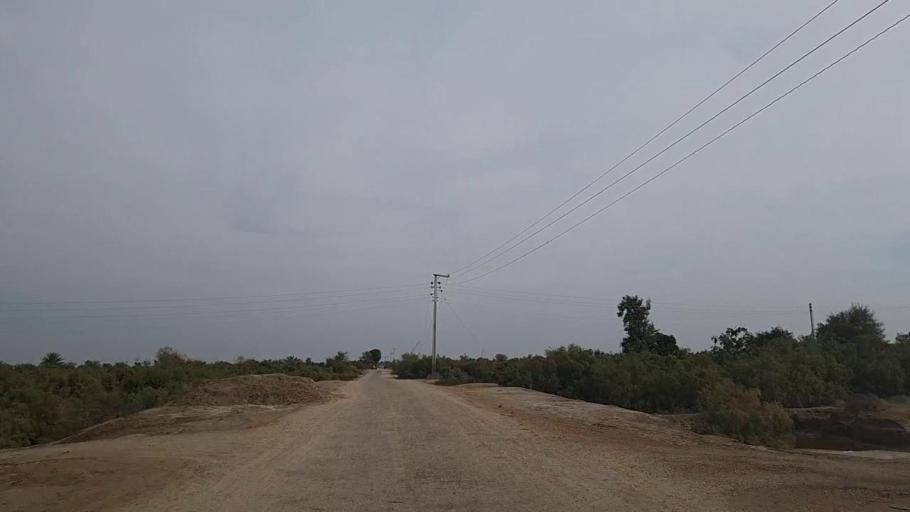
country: PK
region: Sindh
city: Jam Sahib
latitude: 26.4000
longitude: 68.5319
